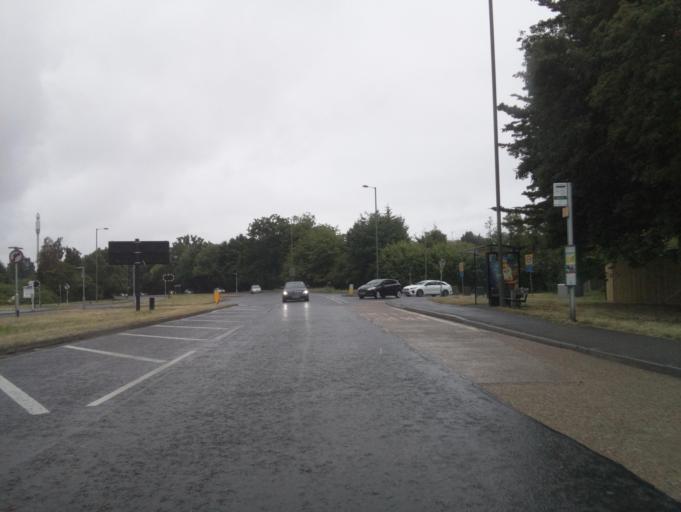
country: GB
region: England
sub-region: Surrey
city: Salfords
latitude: 51.2015
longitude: -0.1669
